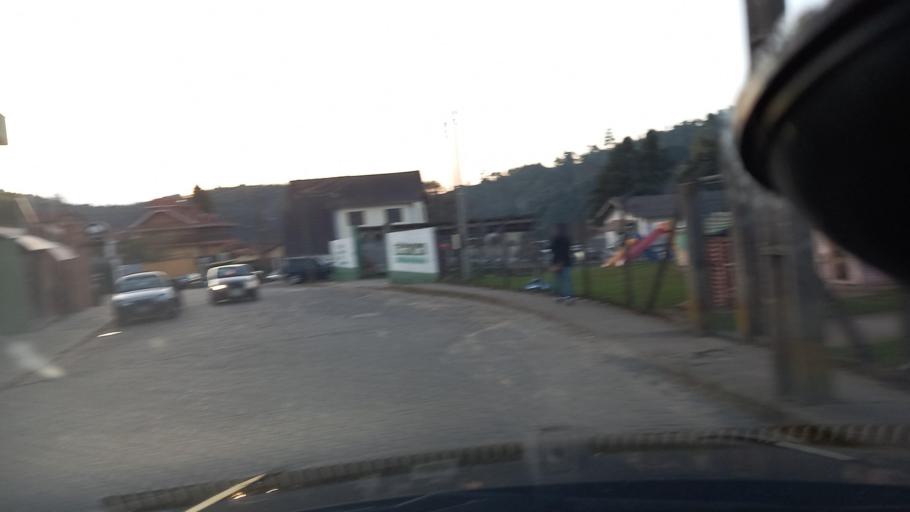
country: BR
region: Minas Gerais
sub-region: Camanducaia
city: Camanducaia
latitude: -22.8579
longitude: -46.0305
